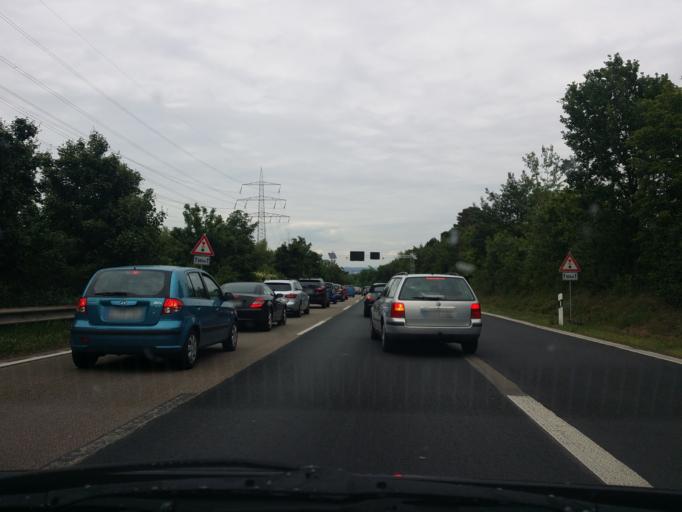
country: DE
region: Rheinland-Pfalz
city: Budenheim
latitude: 50.0139
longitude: 8.2040
